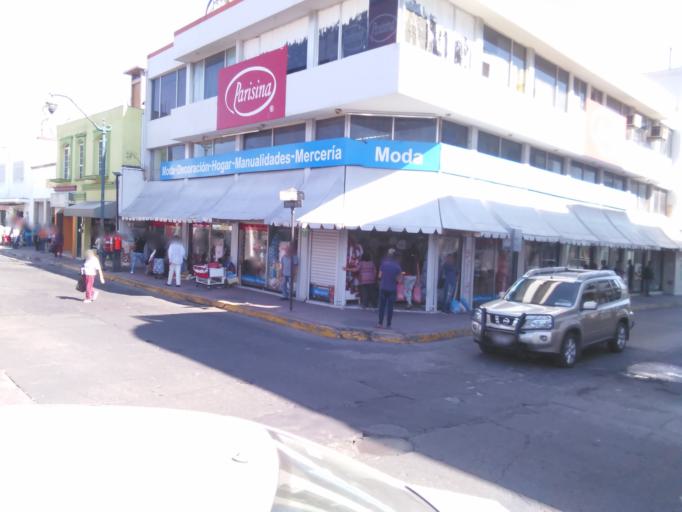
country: MX
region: Nayarit
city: Tepic
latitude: 21.5100
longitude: -104.8945
